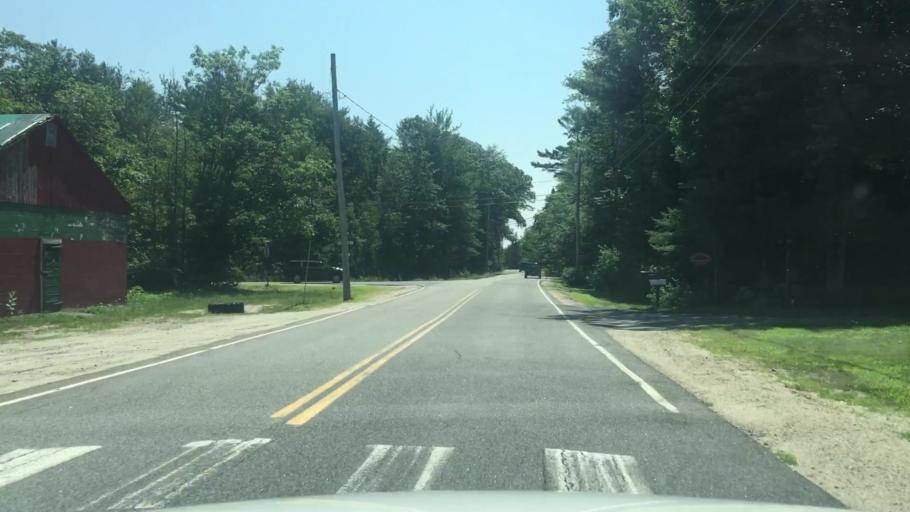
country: US
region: Maine
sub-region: Cumberland County
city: Cumberland Center
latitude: 43.8345
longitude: -70.3023
